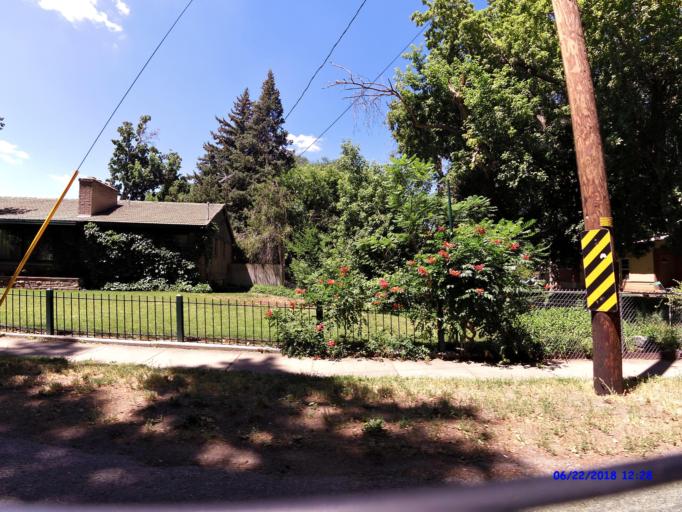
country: US
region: Utah
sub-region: Weber County
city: Ogden
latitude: 41.2404
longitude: -111.9608
